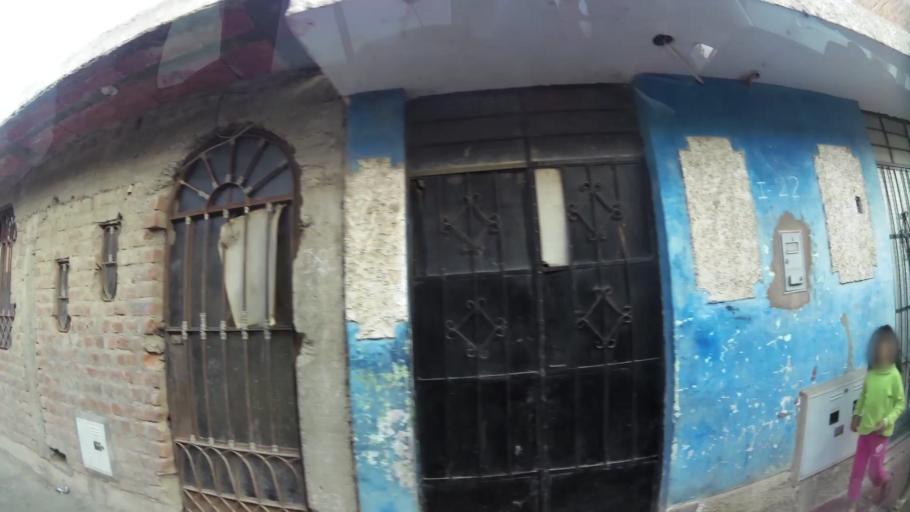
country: PE
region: Ica
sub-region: Provincia de Ica
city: Ica
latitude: -14.0574
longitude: -75.7279
